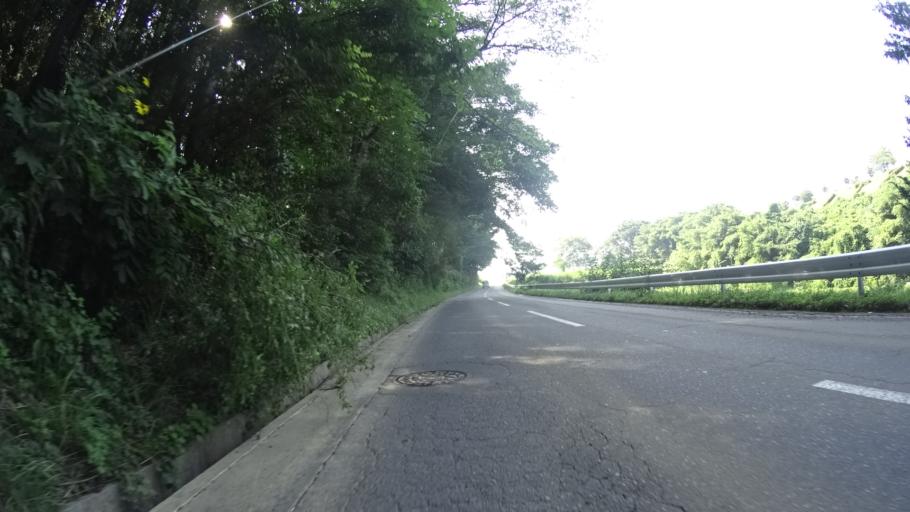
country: JP
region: Nagano
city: Chino
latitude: 35.9729
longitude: 138.1822
